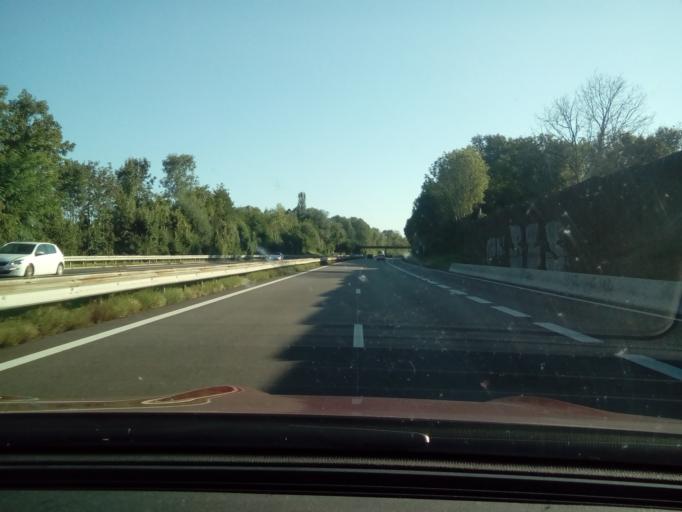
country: FR
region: Rhone-Alpes
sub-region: Departement de la Haute-Savoie
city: Saint-Felix
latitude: 45.8070
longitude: 5.9826
